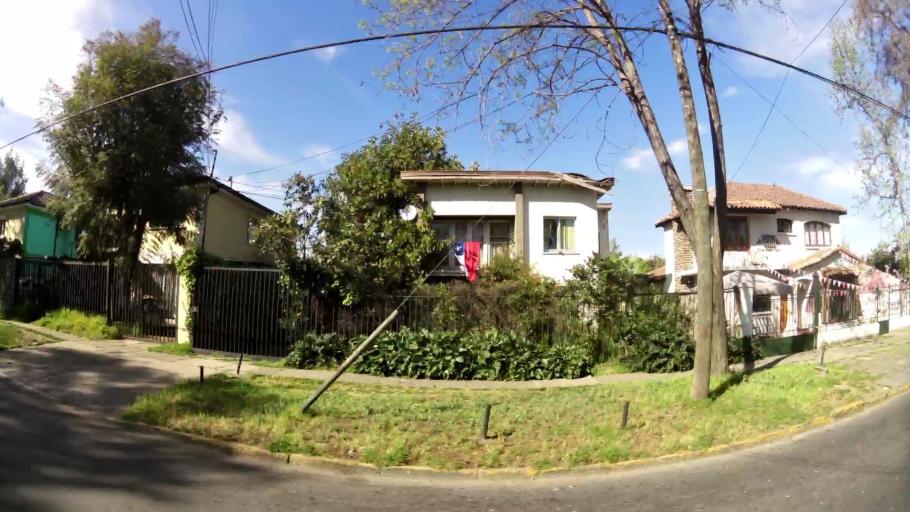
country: CL
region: Santiago Metropolitan
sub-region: Provincia de Santiago
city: Villa Presidente Frei, Nunoa, Santiago, Chile
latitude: -33.4383
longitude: -70.5668
